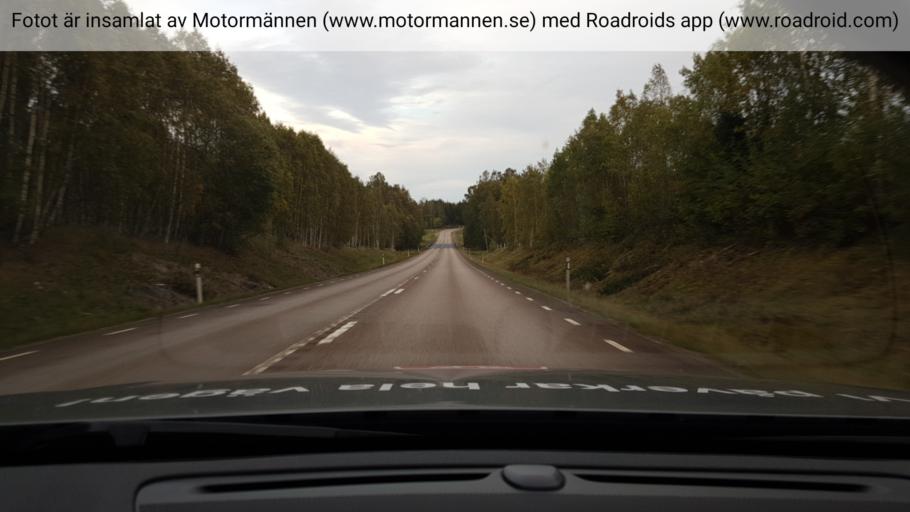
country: SE
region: Vaestra Goetaland
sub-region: Amals Kommun
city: Amal
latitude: 59.0720
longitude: 12.6401
